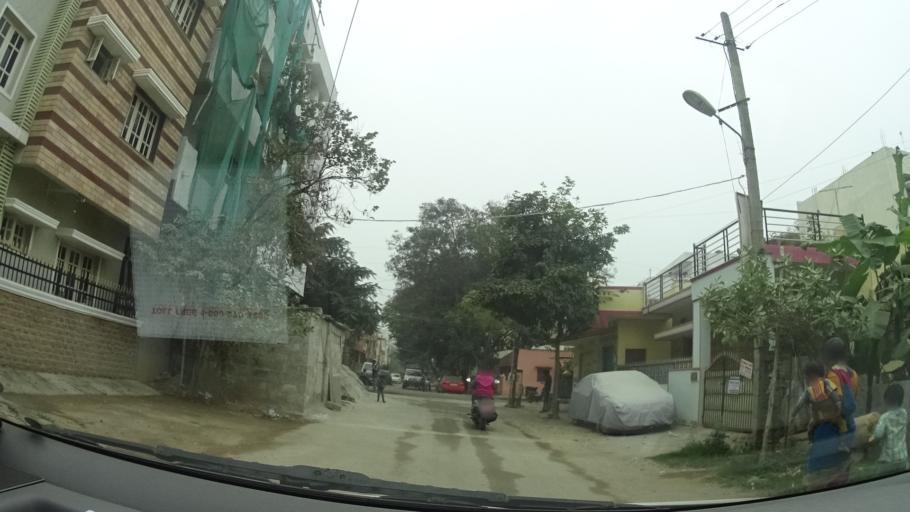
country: IN
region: Karnataka
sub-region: Bangalore Urban
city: Bangalore
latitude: 13.0333
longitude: 77.6333
